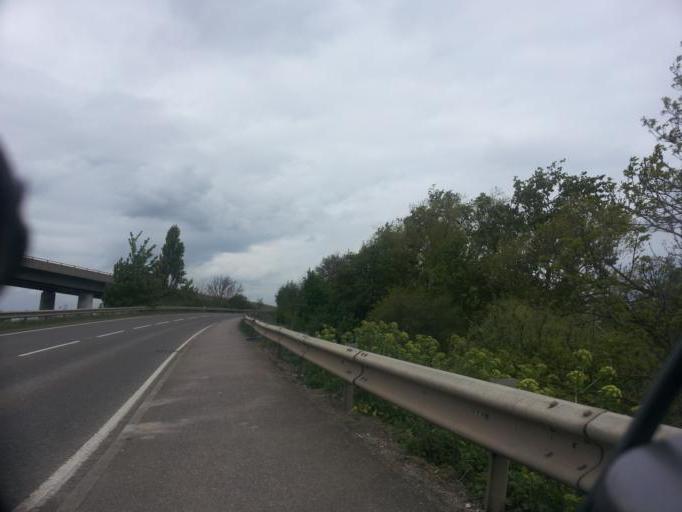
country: GB
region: England
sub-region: Kent
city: Queenborough
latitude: 51.3934
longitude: 0.7537
